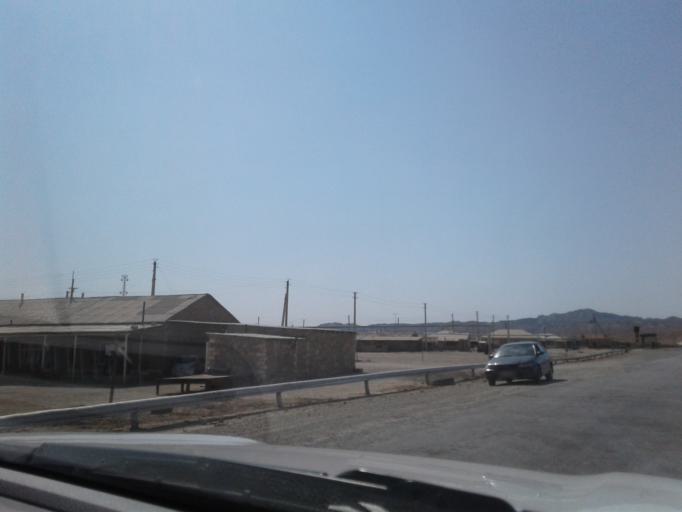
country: TM
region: Balkan
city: Gazanjyk
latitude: 39.1513
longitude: 55.3081
